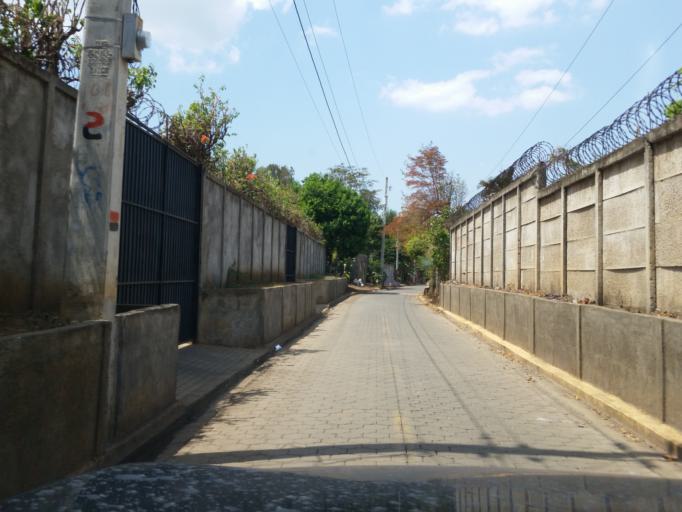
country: NI
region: Masaya
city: Ticuantepe
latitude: 12.0669
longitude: -86.2109
